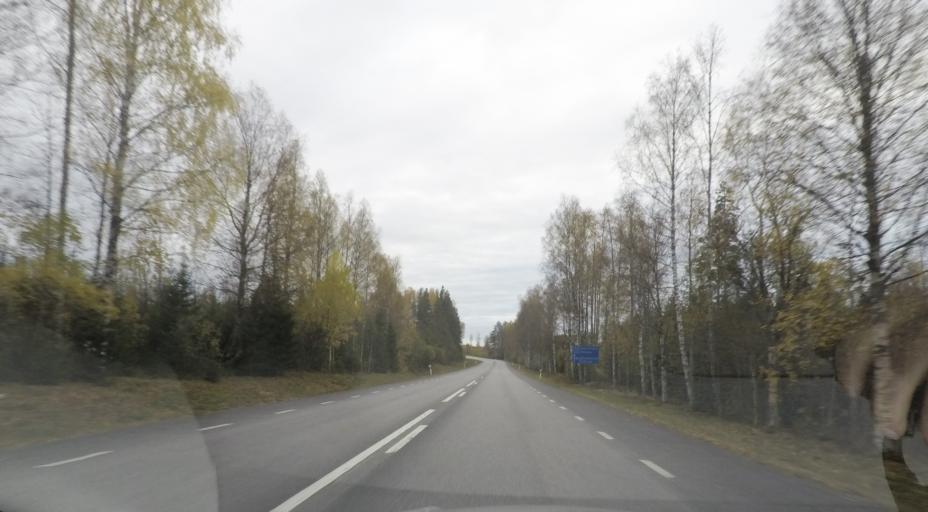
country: SE
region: OErebro
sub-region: Hallefors Kommun
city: Haellefors
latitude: 59.7545
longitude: 14.5110
